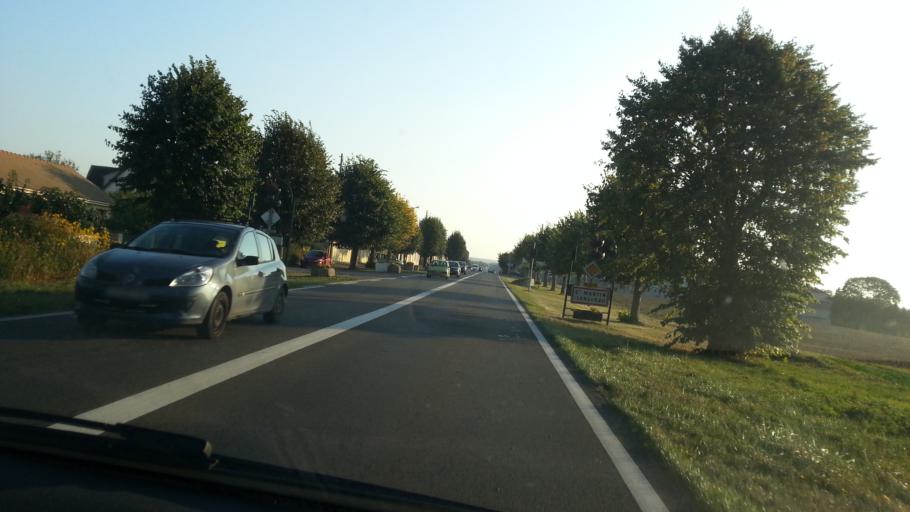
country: FR
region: Picardie
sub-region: Departement de l'Oise
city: Saint-Martin-Longueau
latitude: 49.3464
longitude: 2.6077
